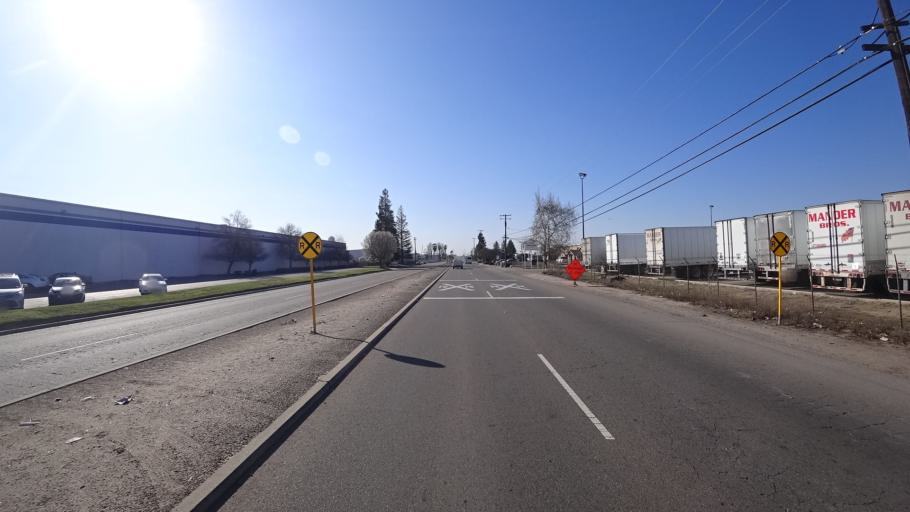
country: US
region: California
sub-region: Fresno County
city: Easton
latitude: 36.6900
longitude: -119.7366
